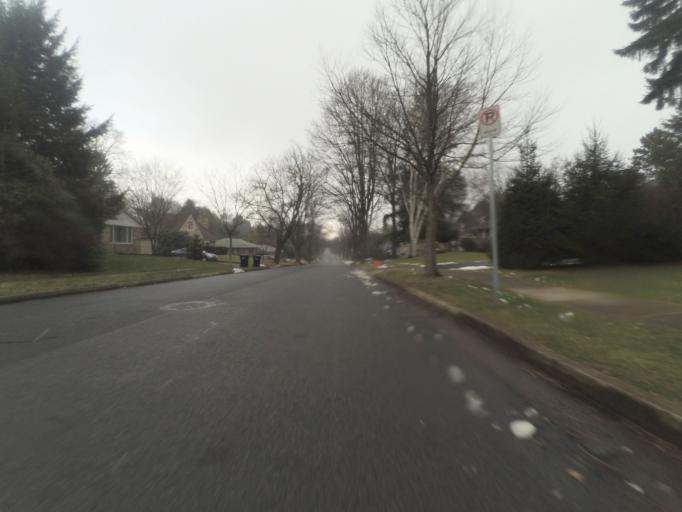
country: US
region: Pennsylvania
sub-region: Centre County
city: State College
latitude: 40.7907
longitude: -77.8503
